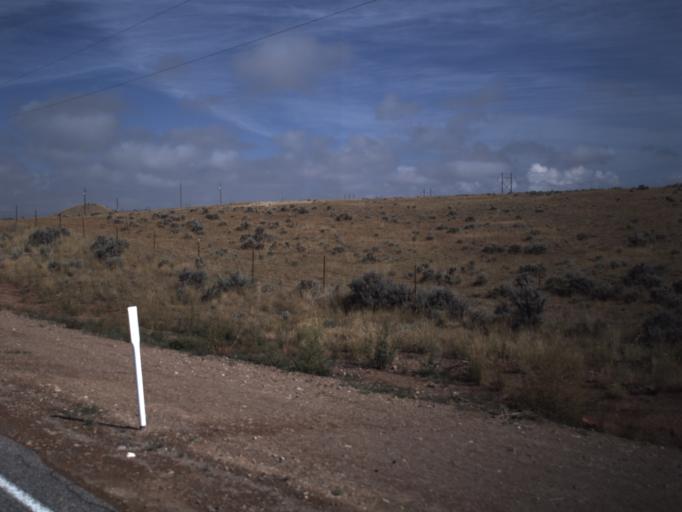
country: US
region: Wyoming
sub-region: Uinta County
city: Evanston
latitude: 41.4213
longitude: -111.0508
